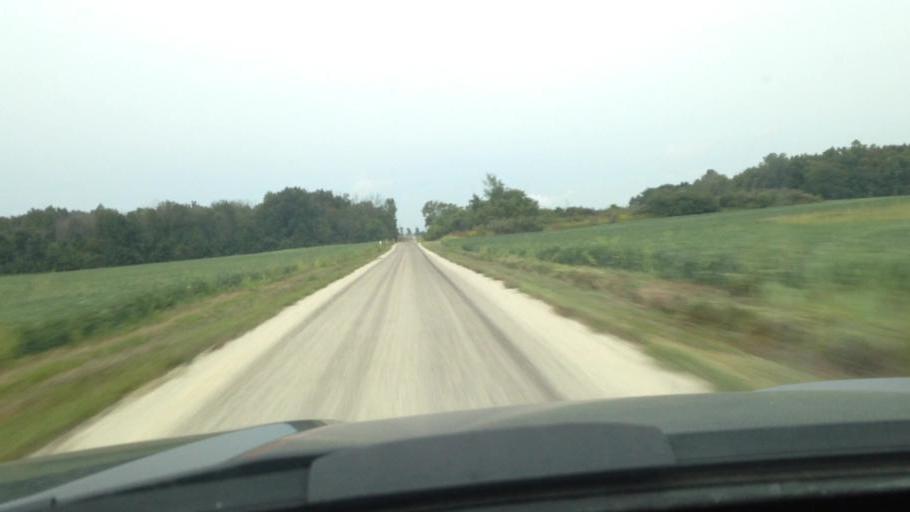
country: US
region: Indiana
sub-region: Randolph County
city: Union City
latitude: 40.2182
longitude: -84.8615
